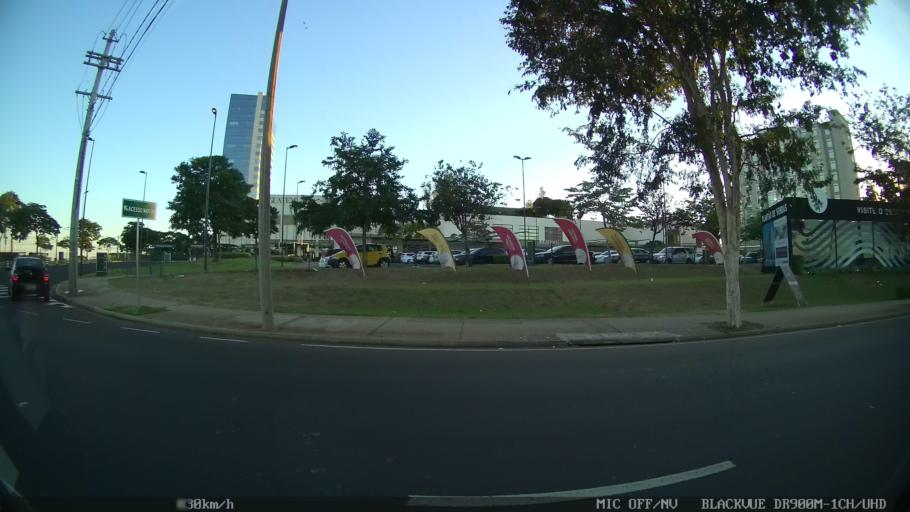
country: BR
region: Sao Paulo
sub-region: Sao Jose Do Rio Preto
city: Sao Jose do Rio Preto
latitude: -20.8654
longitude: -49.4136
